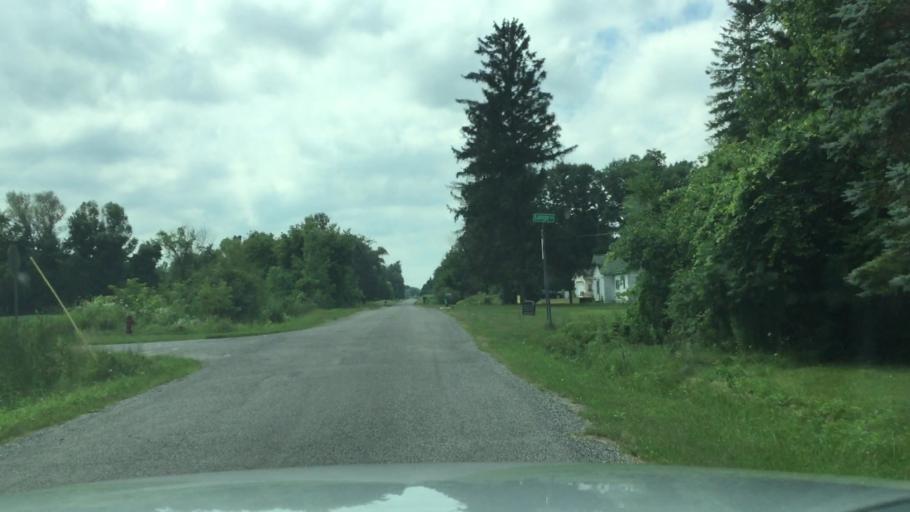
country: US
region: Michigan
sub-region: Saginaw County
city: Birch Run
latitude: 43.3016
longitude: -83.8348
